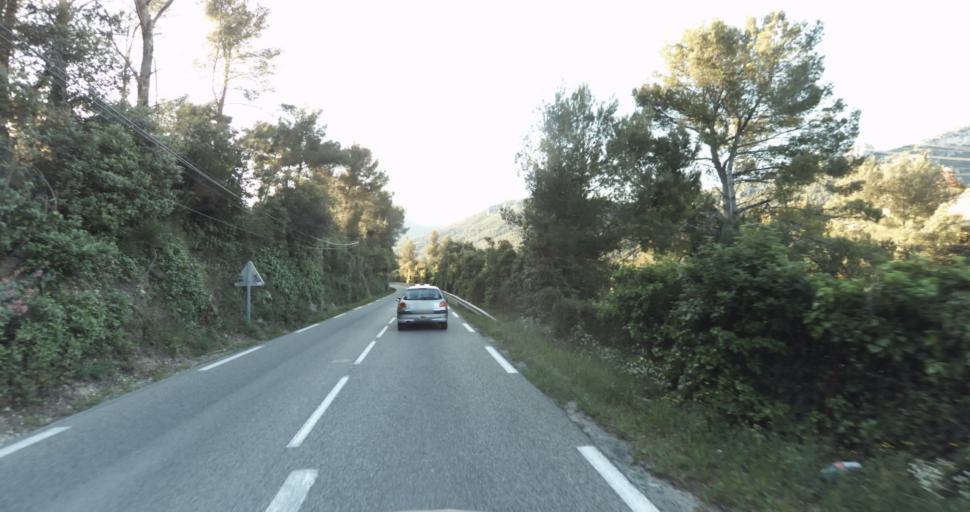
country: FR
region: Provence-Alpes-Cote d'Azur
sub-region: Departement du Var
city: La Valette-du-Var
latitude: 43.1563
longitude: 5.9598
